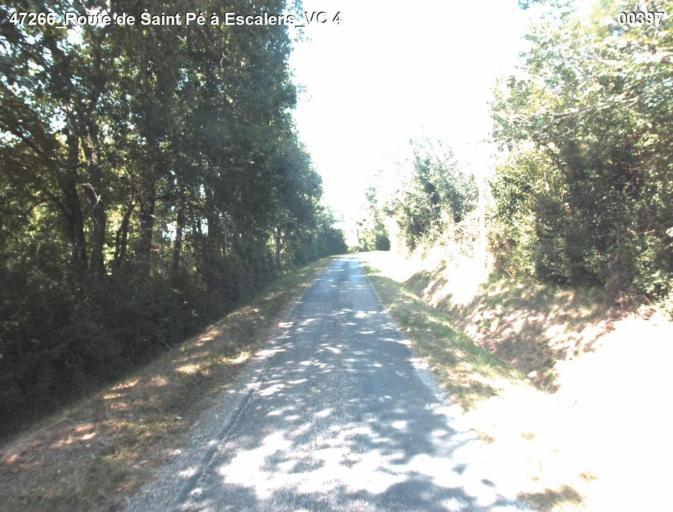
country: FR
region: Aquitaine
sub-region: Departement des Landes
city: Gabarret
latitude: 44.0014
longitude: 0.0666
